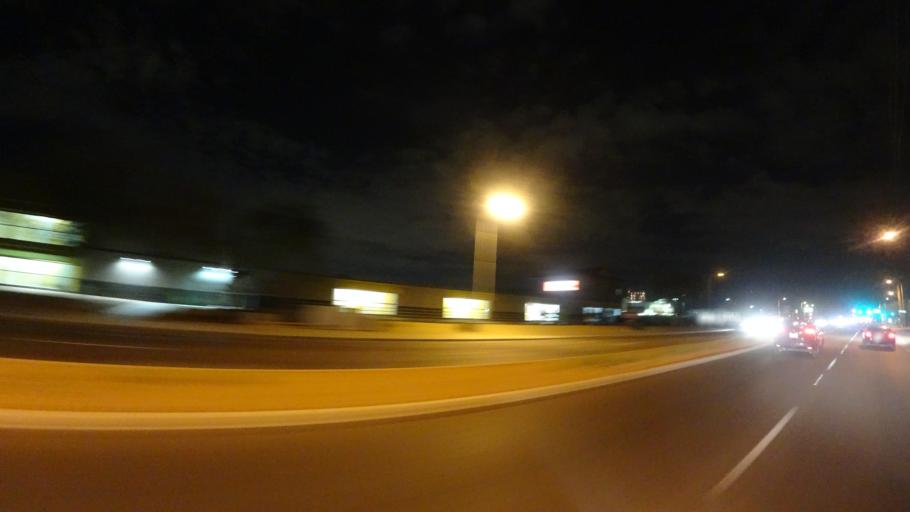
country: US
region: Arizona
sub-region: Maricopa County
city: Tempe
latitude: 33.4200
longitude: -111.9090
